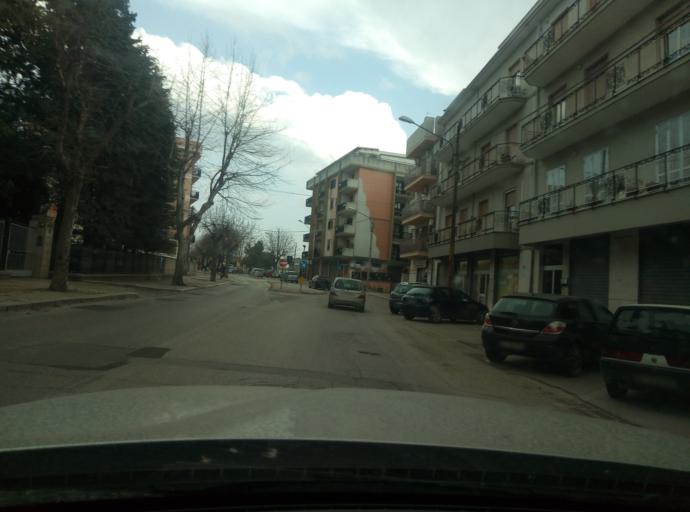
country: IT
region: Apulia
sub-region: Provincia di Bari
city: Ruvo di Puglia
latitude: 41.1125
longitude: 16.4835
